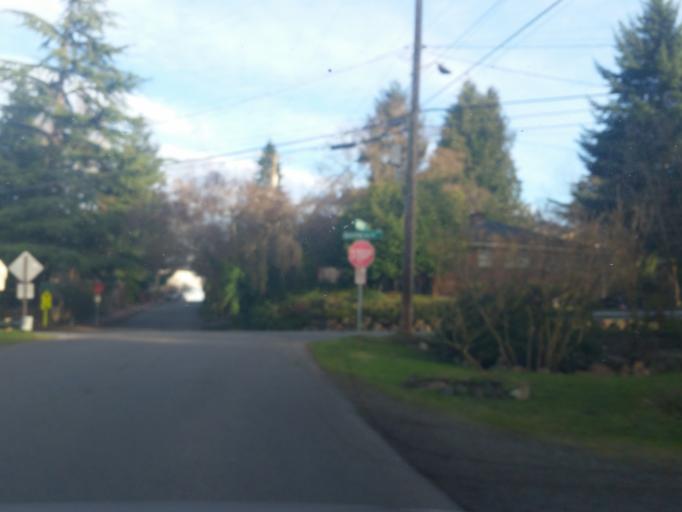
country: US
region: Washington
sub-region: King County
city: Lake Forest Park
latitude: 47.7048
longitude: -122.2980
